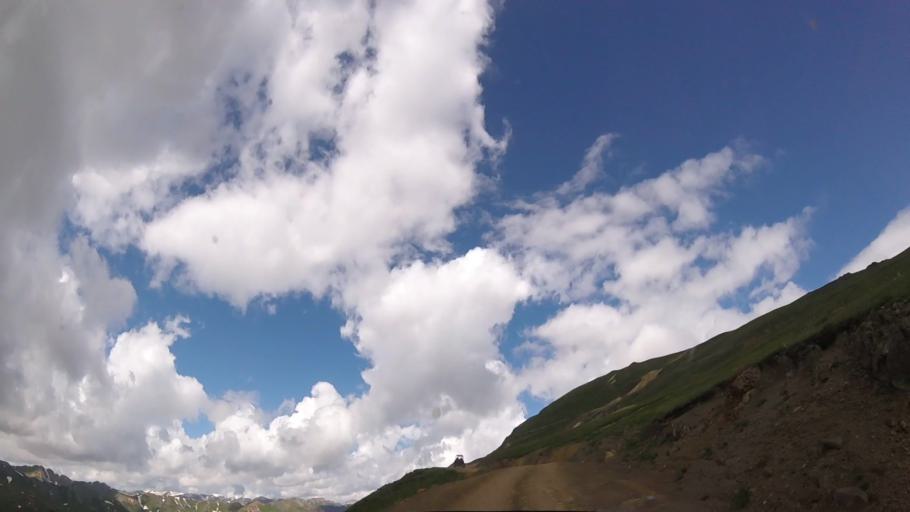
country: US
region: Colorado
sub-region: Ouray County
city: Ouray
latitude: 37.9624
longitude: -107.5761
